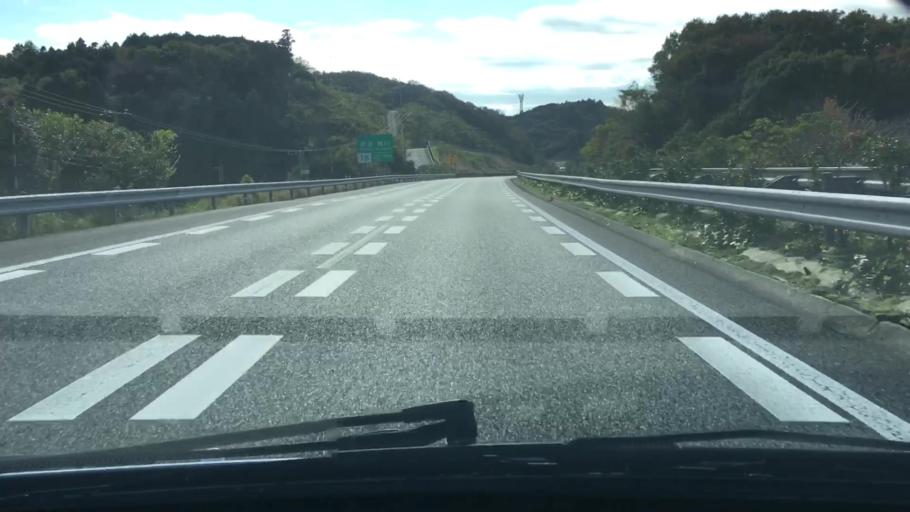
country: JP
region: Chiba
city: Kisarazu
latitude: 35.3307
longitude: 139.9461
